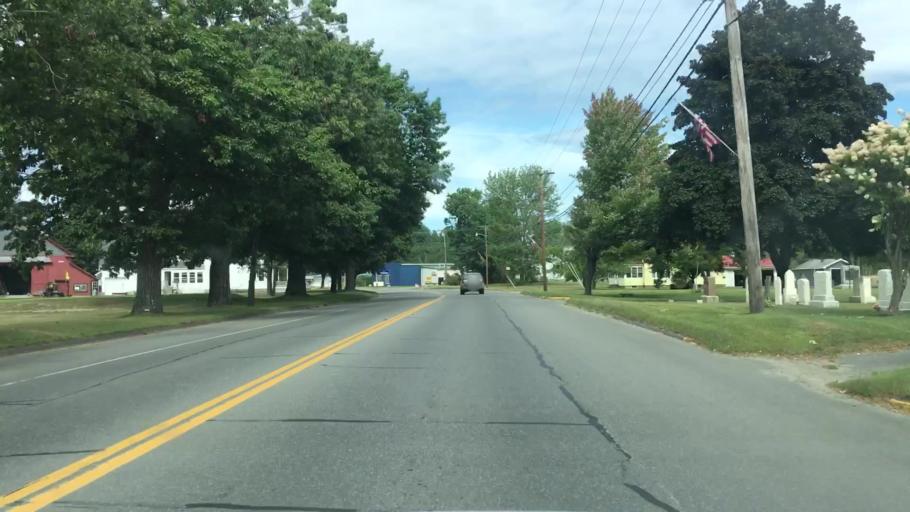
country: US
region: Maine
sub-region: Piscataquis County
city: Milo
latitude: 45.2596
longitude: -68.9878
